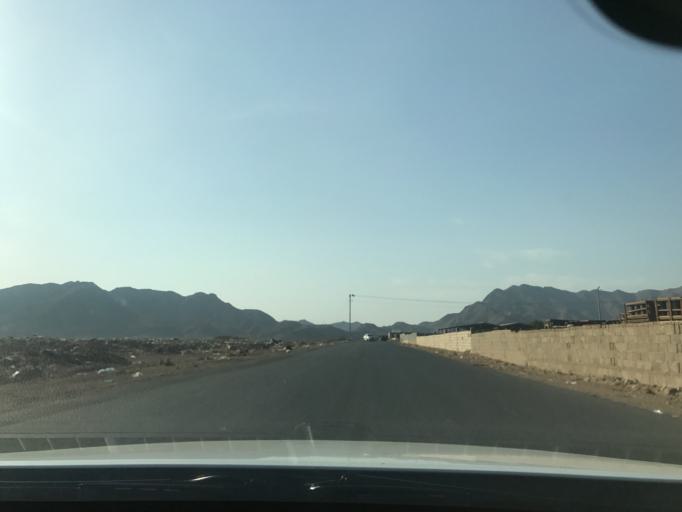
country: SA
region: Makkah
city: Al Jumum
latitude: 21.4404
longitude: 39.5161
